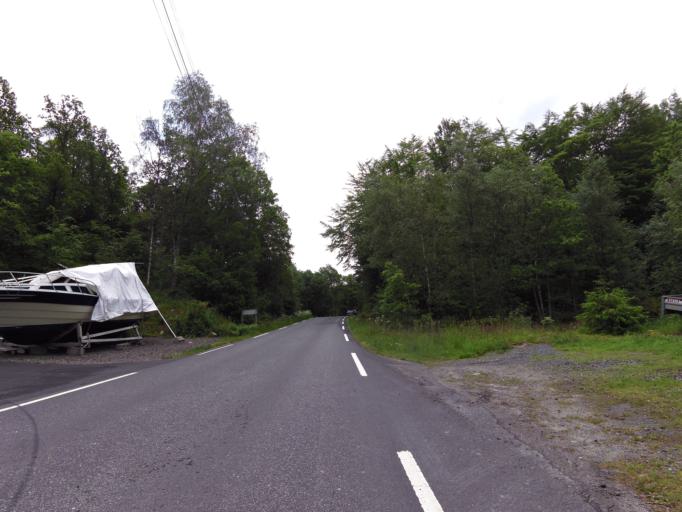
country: NO
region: Vest-Agder
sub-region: Lyngdal
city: Lyngdal
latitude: 58.1103
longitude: 6.9596
